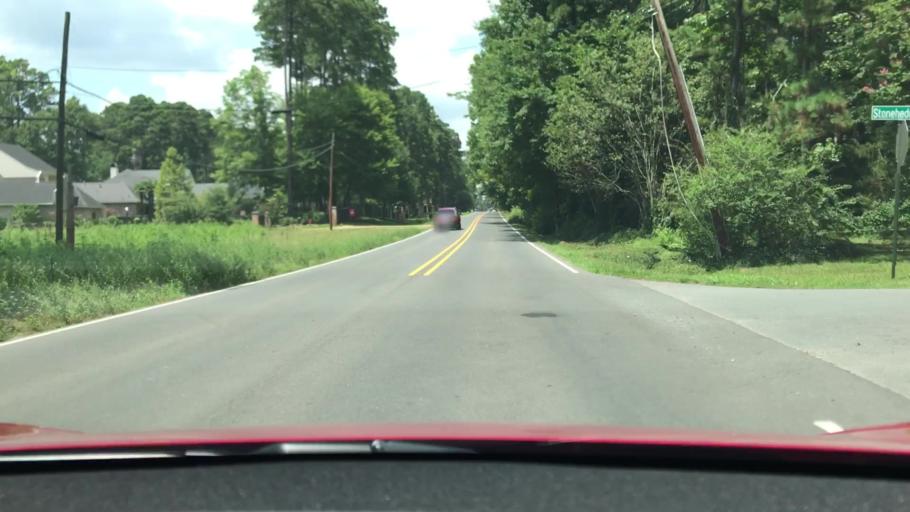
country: US
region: Louisiana
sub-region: Bossier Parish
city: Bossier City
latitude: 32.3776
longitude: -93.7138
